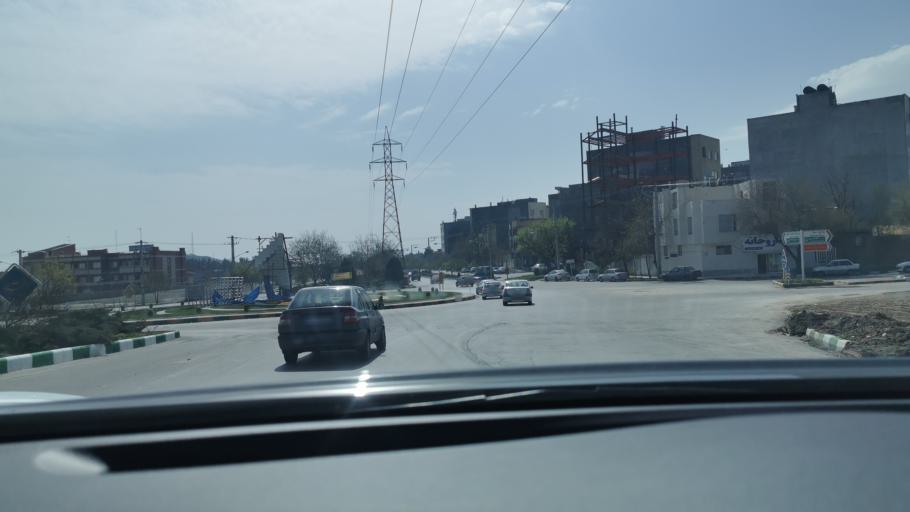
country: IR
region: Razavi Khorasan
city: Mashhad
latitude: 36.2834
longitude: 59.5435
